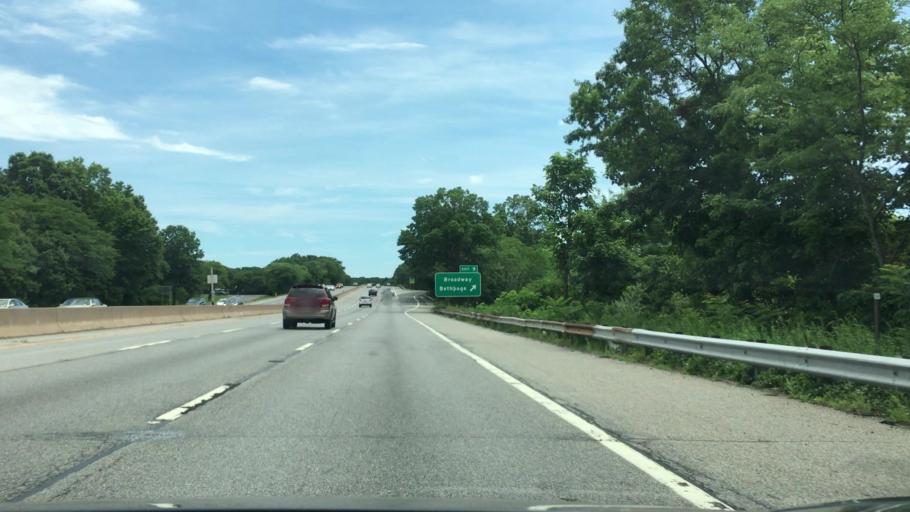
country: US
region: New York
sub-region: Nassau County
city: Bethpage
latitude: 40.7598
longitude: -73.4763
